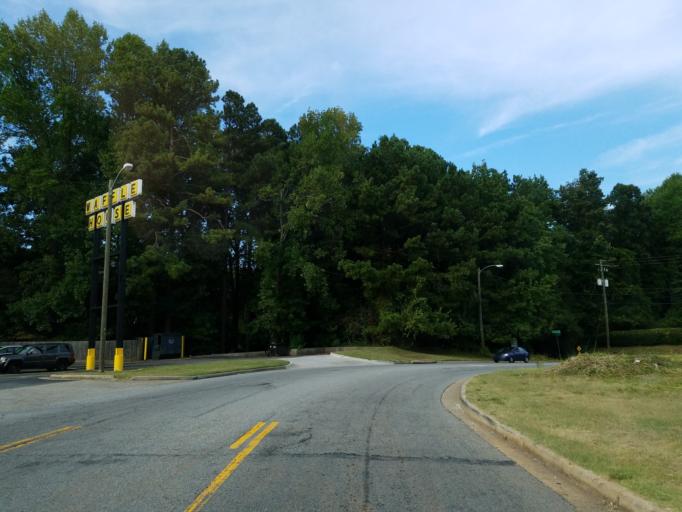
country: US
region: Georgia
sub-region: Cobb County
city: Marietta
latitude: 33.9981
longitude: -84.5294
